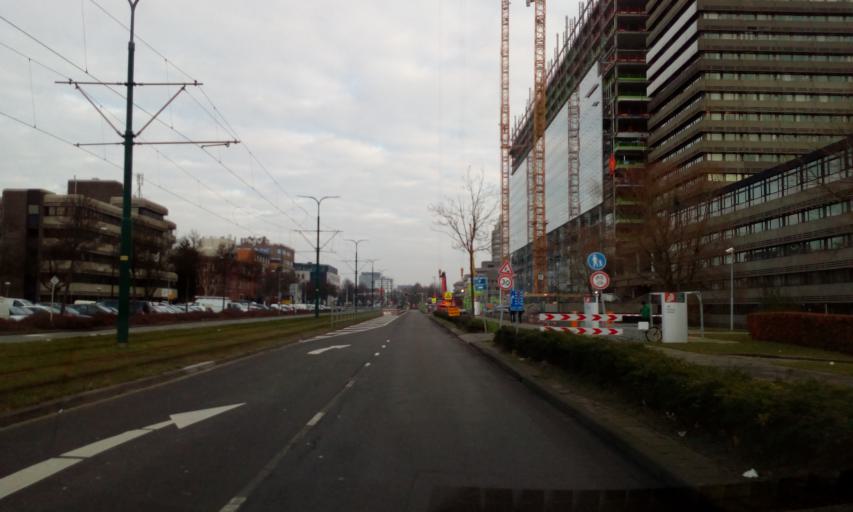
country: NL
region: South Holland
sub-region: Gemeente Rijswijk
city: Rijswijk
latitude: 52.0395
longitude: 4.3357
